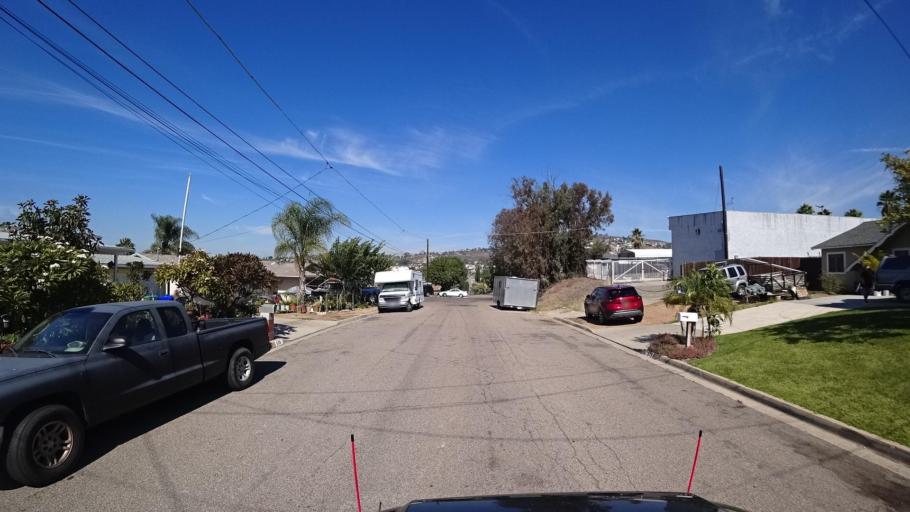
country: US
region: California
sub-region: San Diego County
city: La Presa
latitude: 32.7071
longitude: -117.0010
